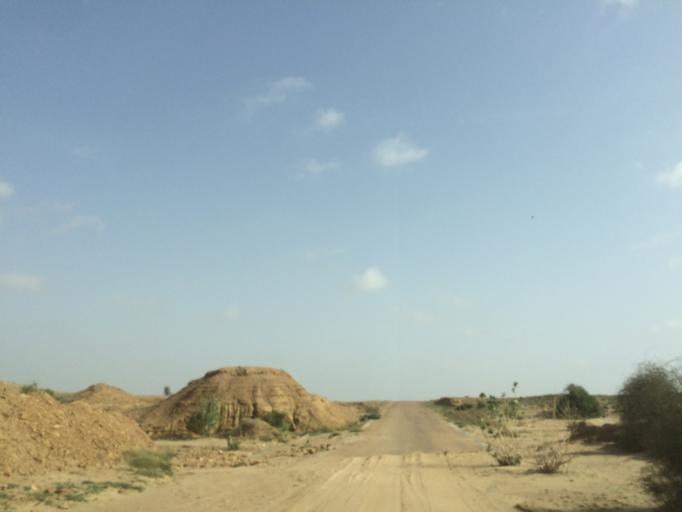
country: IN
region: Rajasthan
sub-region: Jaisalmer
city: Jaisalmer
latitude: 26.7786
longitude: 70.6872
